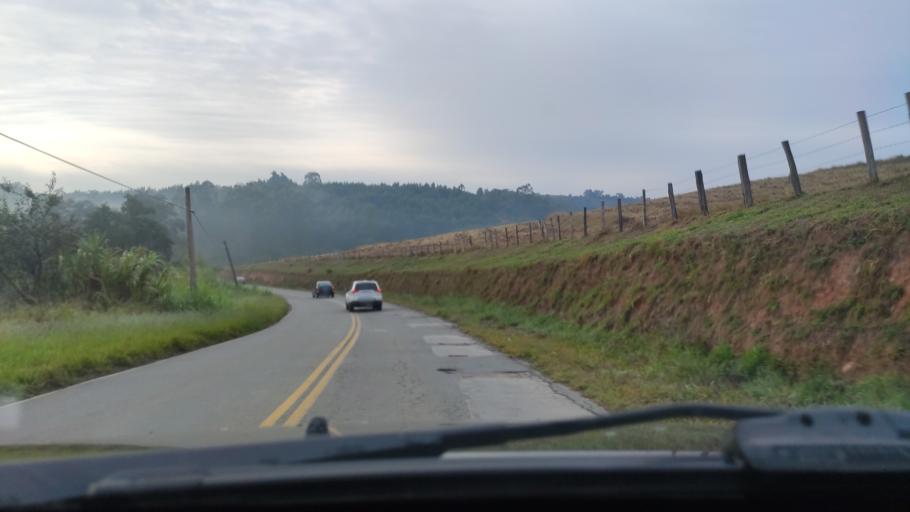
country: BR
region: Sao Paulo
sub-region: Jarinu
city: Jarinu
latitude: -23.1336
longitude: -46.7800
